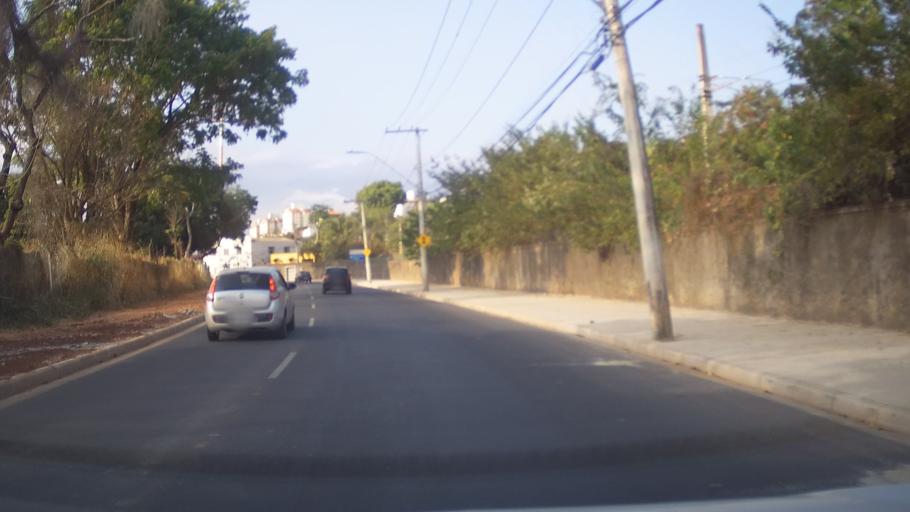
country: BR
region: Minas Gerais
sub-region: Belo Horizonte
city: Belo Horizonte
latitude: -19.8887
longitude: -43.9124
